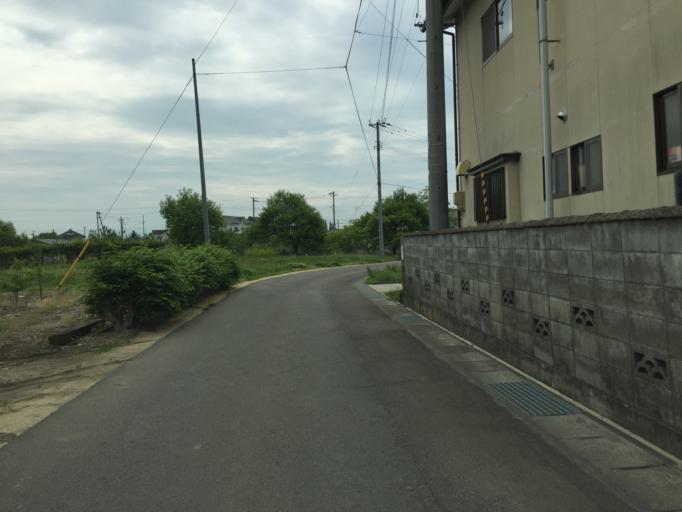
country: JP
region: Fukushima
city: Fukushima-shi
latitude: 37.8134
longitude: 140.4361
